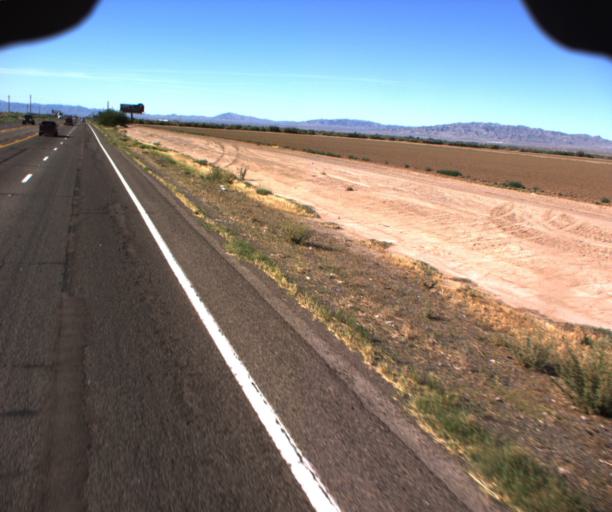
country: US
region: Arizona
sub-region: Mohave County
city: Mohave Valley
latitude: 34.9571
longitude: -114.5980
